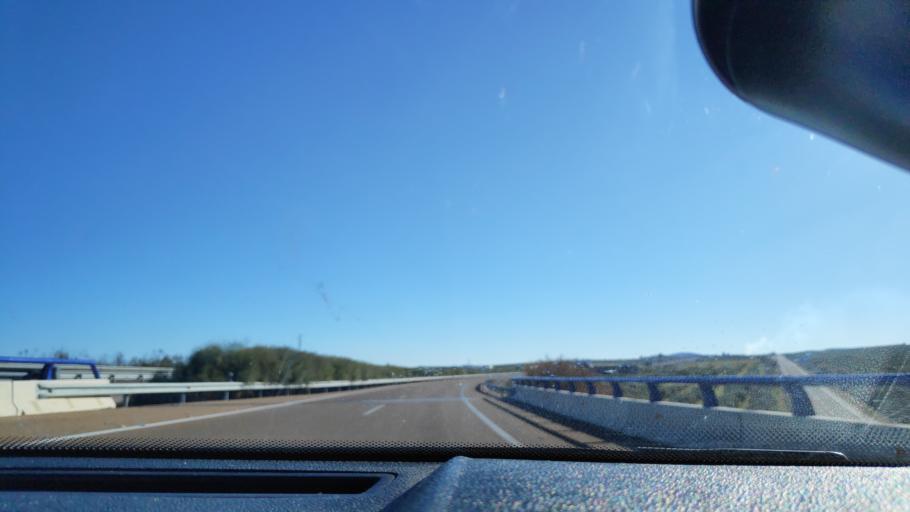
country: ES
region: Extremadura
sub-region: Provincia de Badajoz
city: Villafranca de los Barros
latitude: 38.5264
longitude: -6.3502
